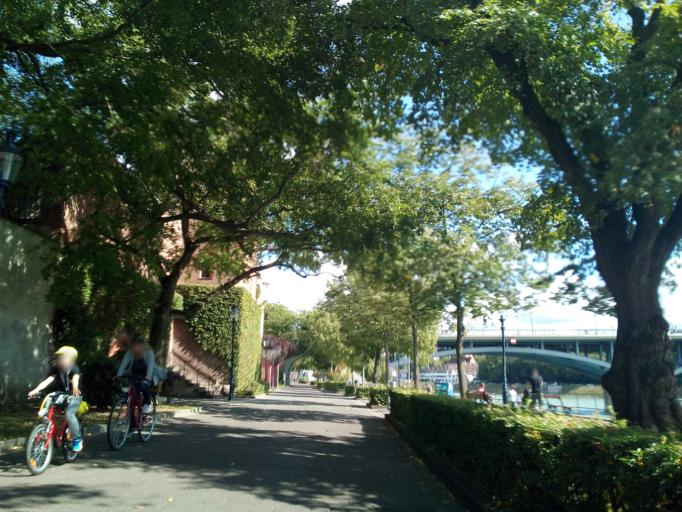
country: CH
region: Basel-City
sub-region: Basel-Stadt
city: Basel
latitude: 47.5583
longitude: 7.5948
